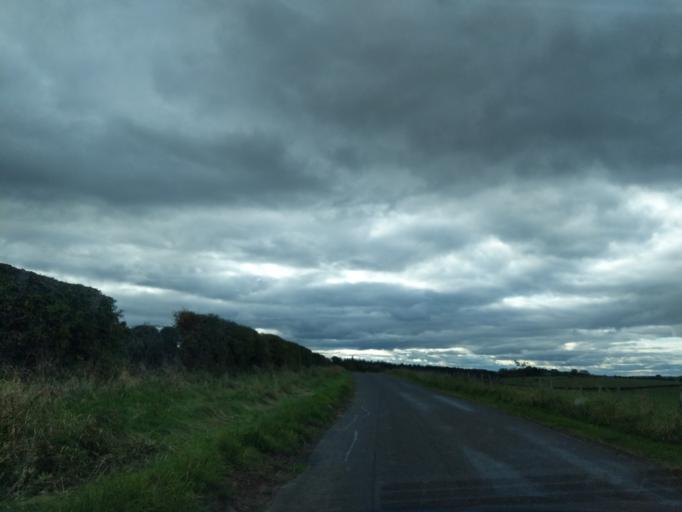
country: GB
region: Scotland
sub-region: East Lothian
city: East Linton
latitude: 55.9396
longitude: -2.7116
